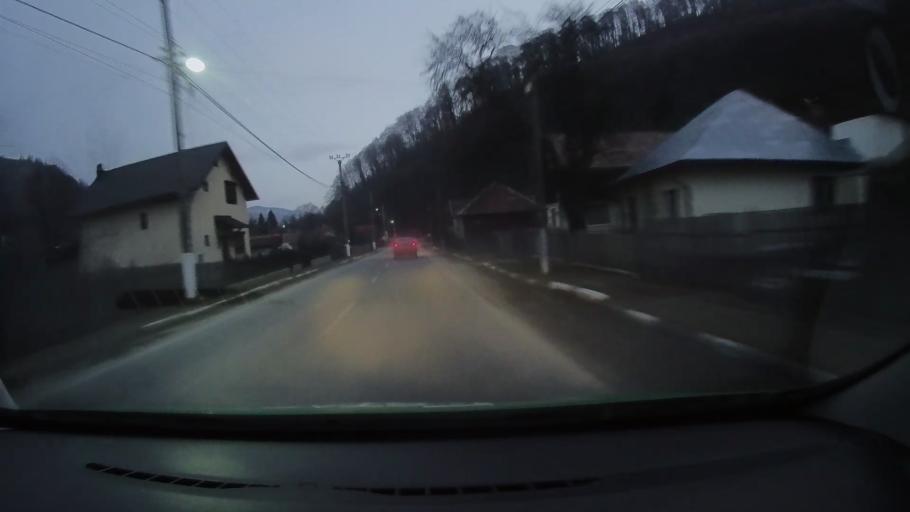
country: RO
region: Prahova
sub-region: Comuna Valea Doftanei
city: Tesila
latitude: 45.2842
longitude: 25.7235
